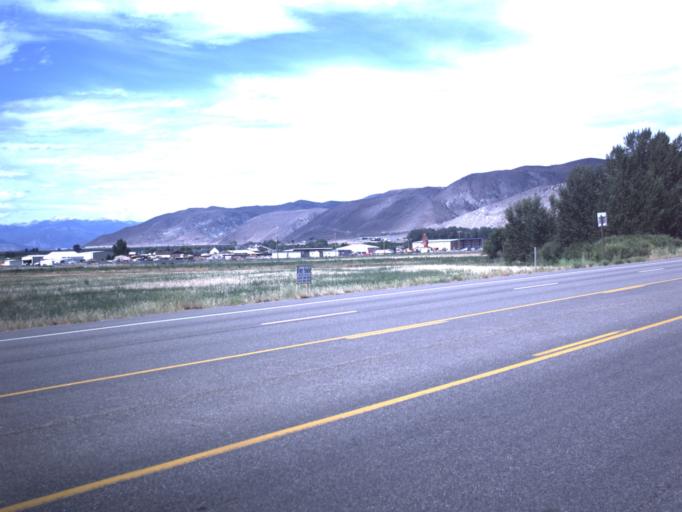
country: US
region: Utah
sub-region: Sevier County
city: Richfield
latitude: 38.7497
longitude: -112.0918
